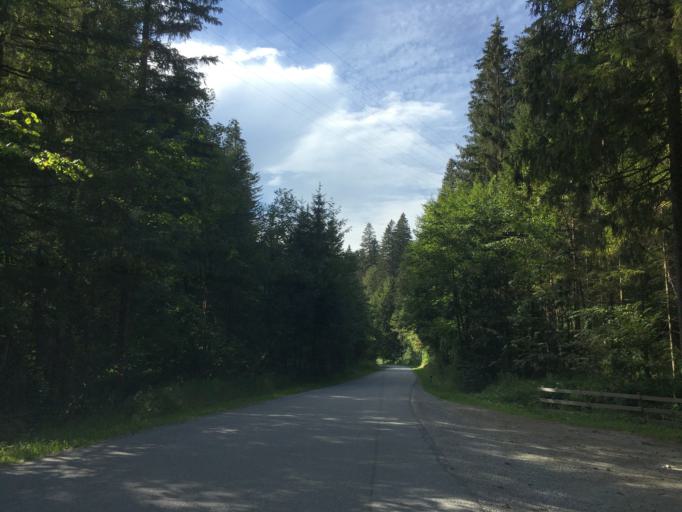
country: AT
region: Salzburg
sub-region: Politischer Bezirk Hallein
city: Abtenau
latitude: 47.5254
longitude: 13.4336
